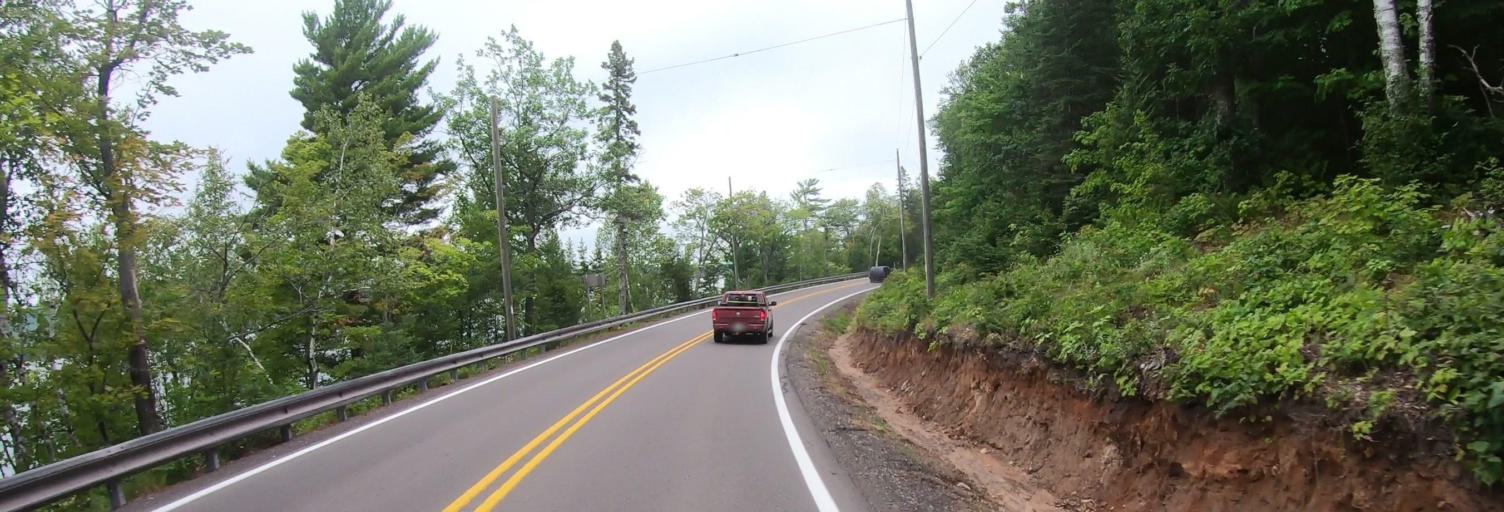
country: US
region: Michigan
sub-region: Keweenaw County
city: Eagle River
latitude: 47.4343
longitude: -87.9792
